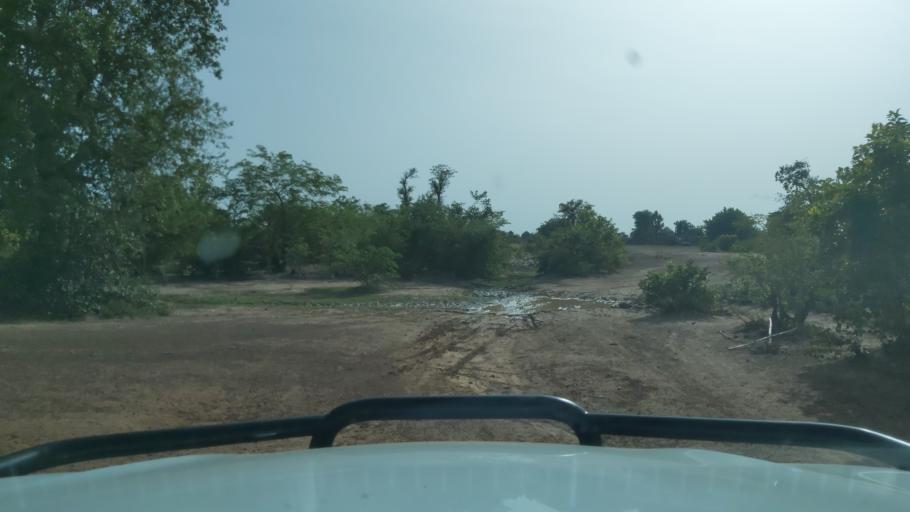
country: ML
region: Koulikoro
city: Koulikoro
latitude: 13.1651
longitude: -7.7917
